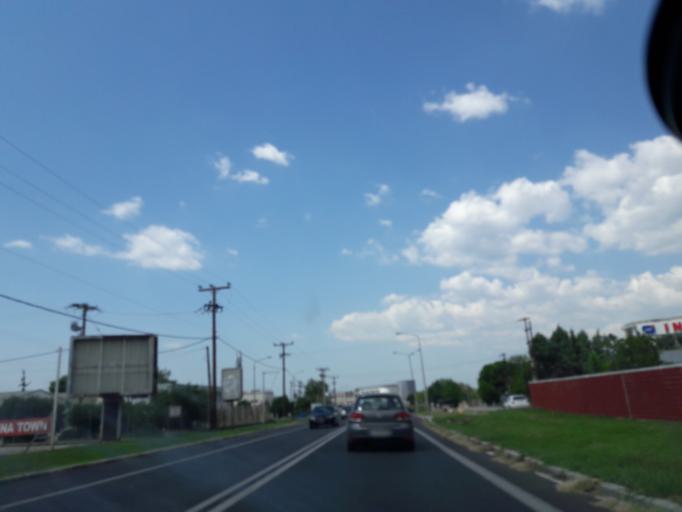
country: GR
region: Central Macedonia
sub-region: Nomos Thessalonikis
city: Thermi
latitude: 40.5401
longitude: 23.0301
